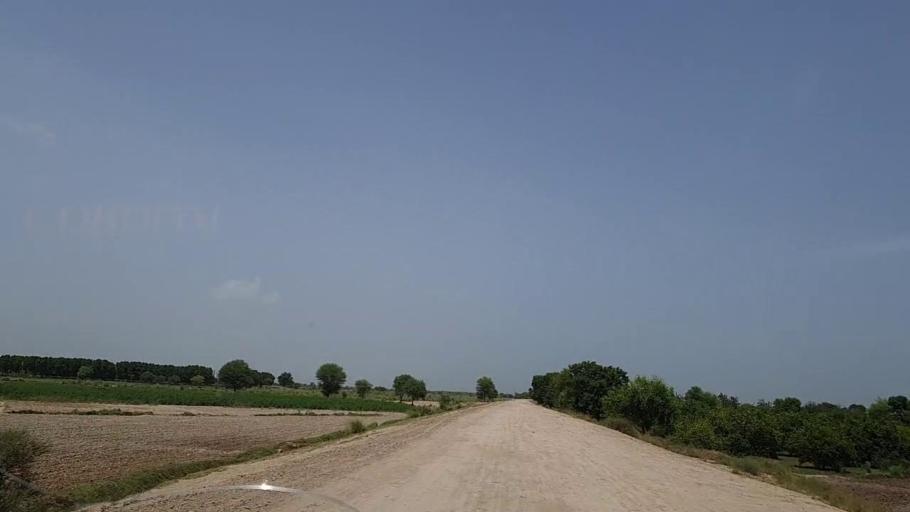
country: PK
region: Sindh
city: Kandiaro
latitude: 27.0530
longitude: 68.1224
